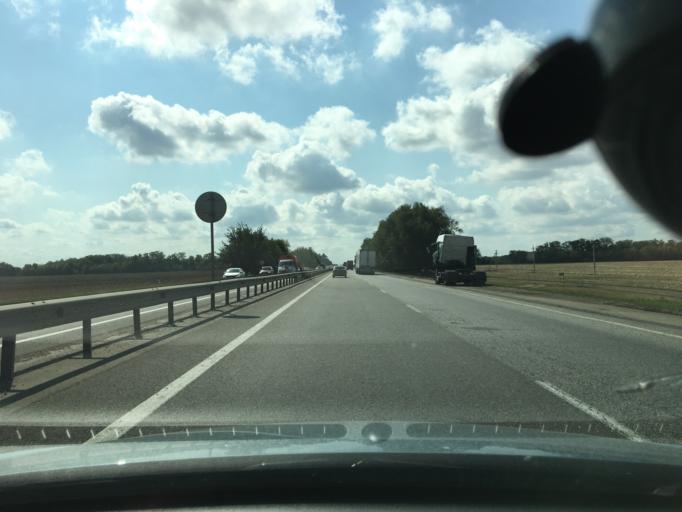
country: RU
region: Krasnodarskiy
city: Krasnoye
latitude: 46.6939
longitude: 39.6517
